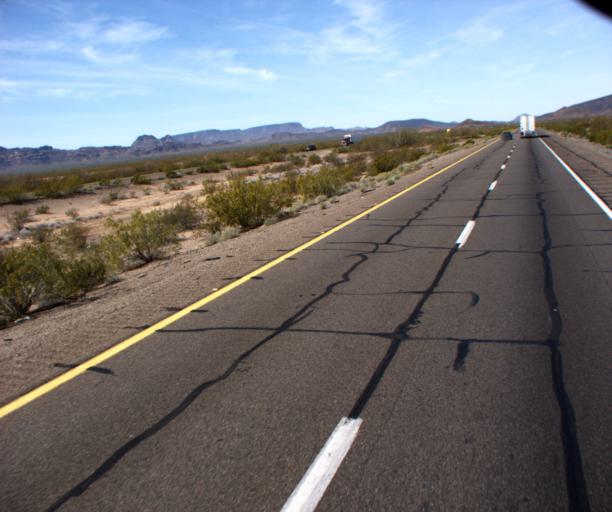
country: US
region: Arizona
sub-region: La Paz County
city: Salome
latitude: 33.6402
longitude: -113.8298
